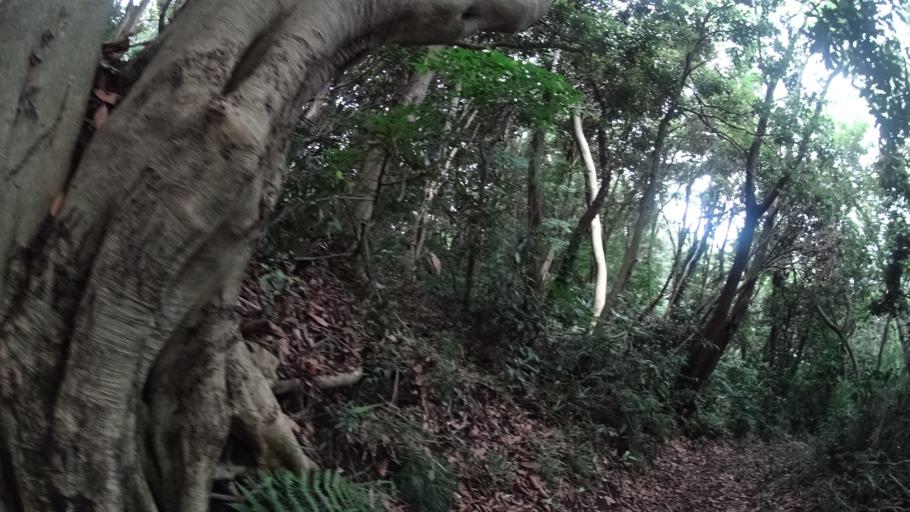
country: JP
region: Kanagawa
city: Yokosuka
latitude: 35.2148
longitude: 139.6563
